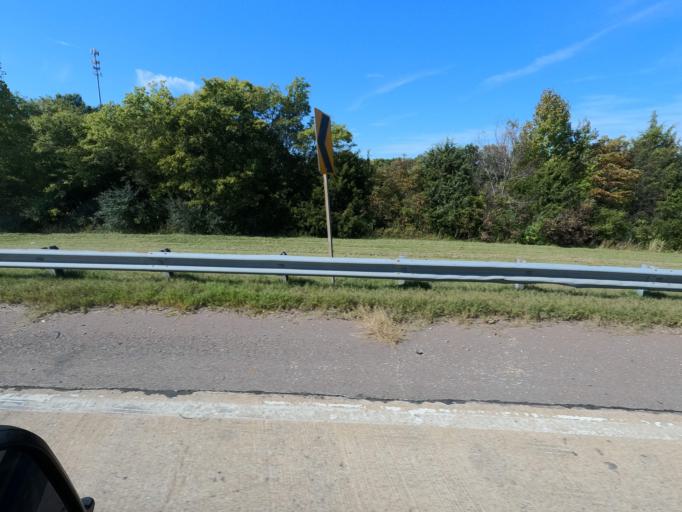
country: US
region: Tennessee
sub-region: Dyer County
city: Dyersburg
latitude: 36.0737
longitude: -89.3509
